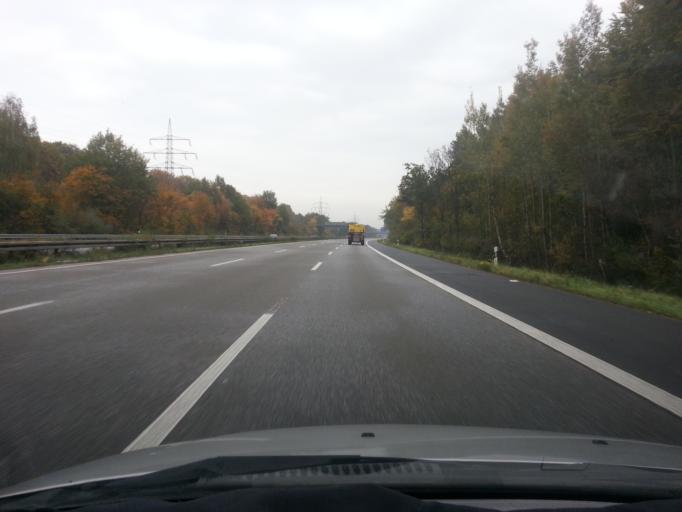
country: DE
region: Hesse
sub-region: Regierungsbezirk Darmstadt
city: Neu Isenburg
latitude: 50.0390
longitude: 8.7149
